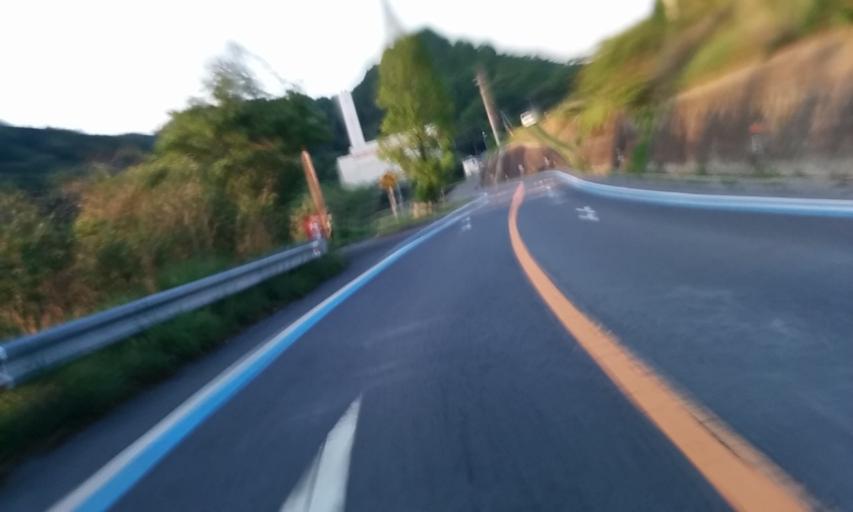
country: JP
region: Ehime
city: Iyo
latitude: 33.7128
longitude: 132.6682
